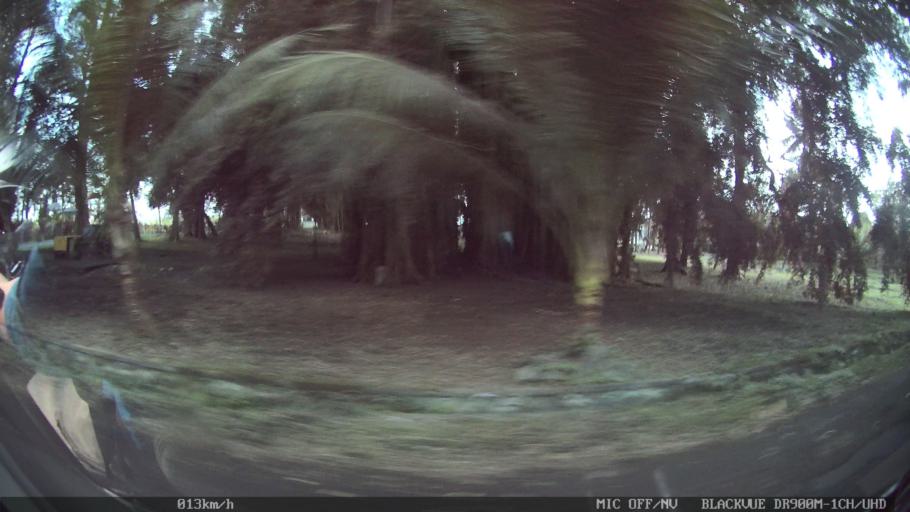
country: ID
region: Bali
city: Banjar Tebongkang
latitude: -8.5325
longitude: 115.2522
